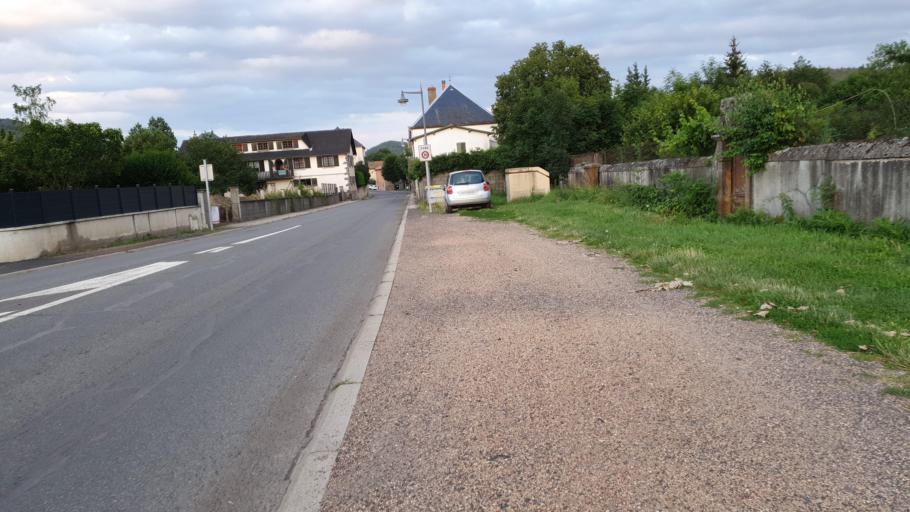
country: FR
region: Auvergne
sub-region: Departement du Puy-de-Dome
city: Aydat
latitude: 45.5731
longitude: 3.0126
